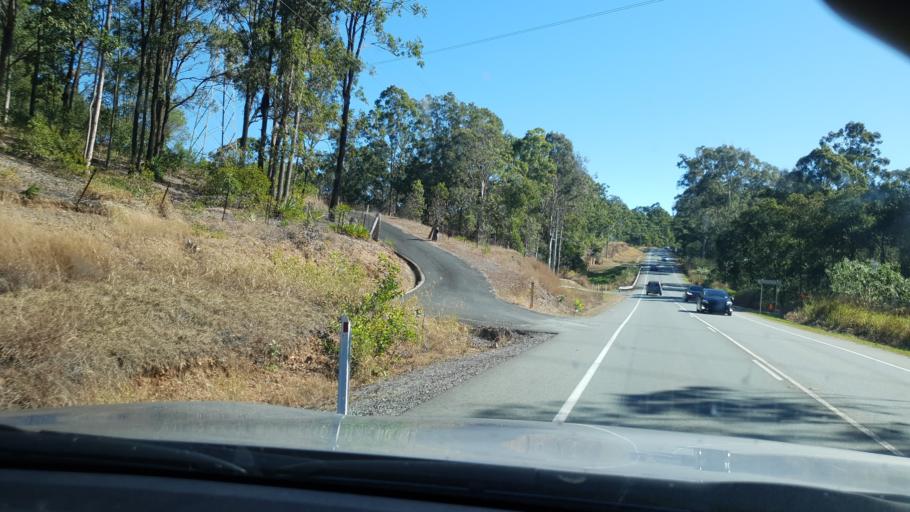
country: AU
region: Queensland
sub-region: Moreton Bay
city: Strathpine
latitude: -27.3295
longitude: 152.9417
